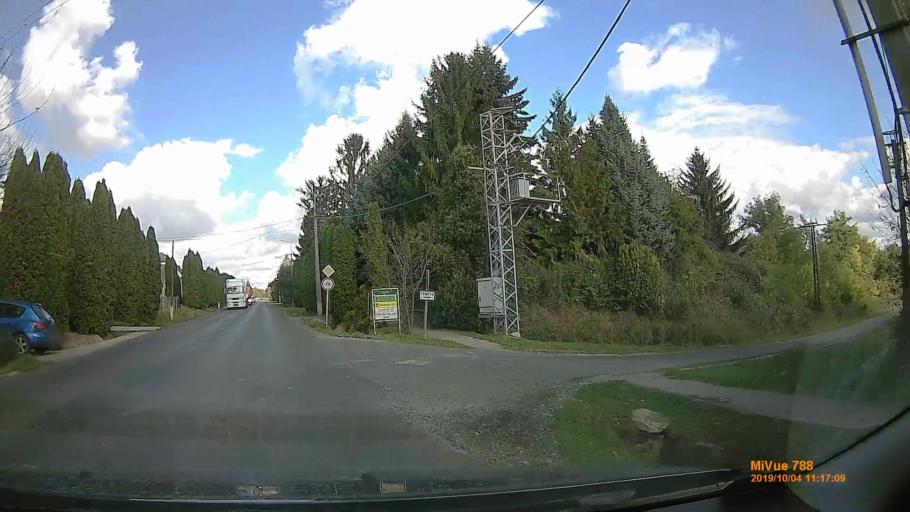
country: HU
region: Somogy
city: Kaposvar
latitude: 46.4606
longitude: 17.8052
